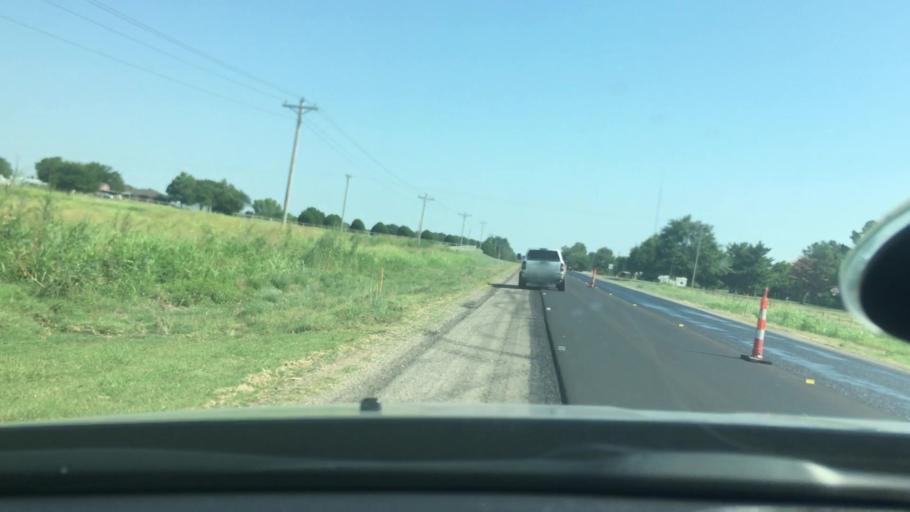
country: US
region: Oklahoma
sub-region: Garvin County
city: Lindsay
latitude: 34.8014
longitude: -97.5983
